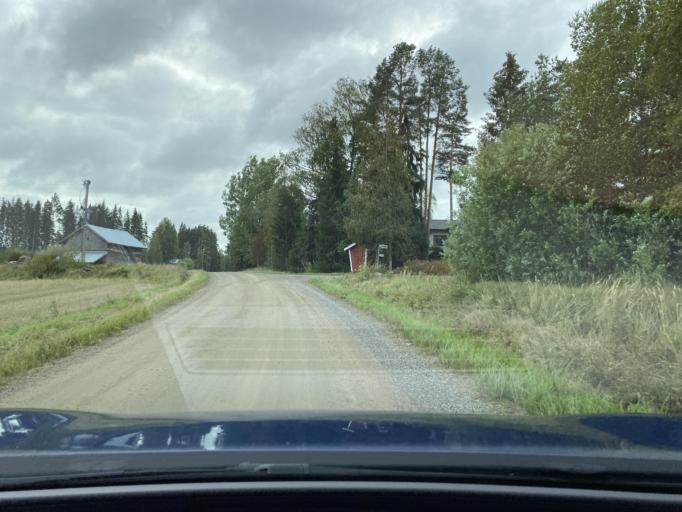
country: FI
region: Pirkanmaa
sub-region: Lounais-Pirkanmaa
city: Punkalaidun
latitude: 61.1805
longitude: 23.1824
